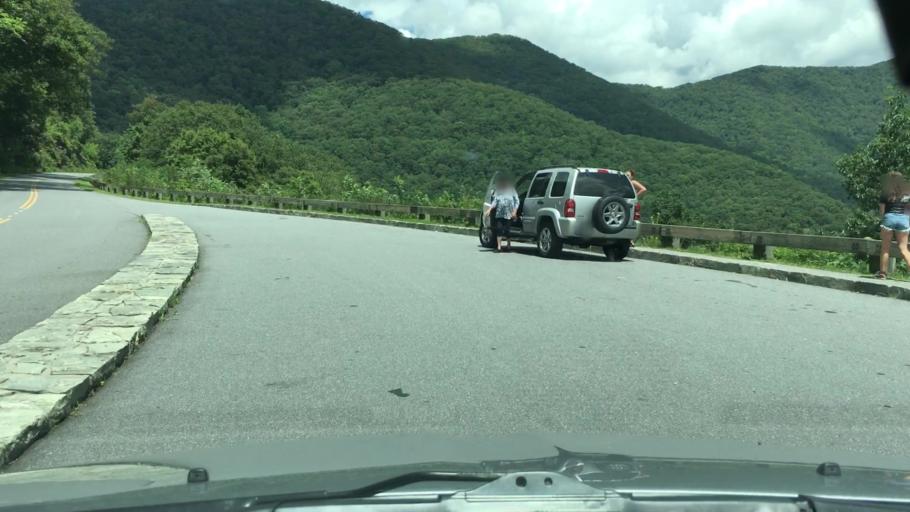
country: US
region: North Carolina
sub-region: Buncombe County
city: Swannanoa
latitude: 35.6680
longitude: -82.4423
